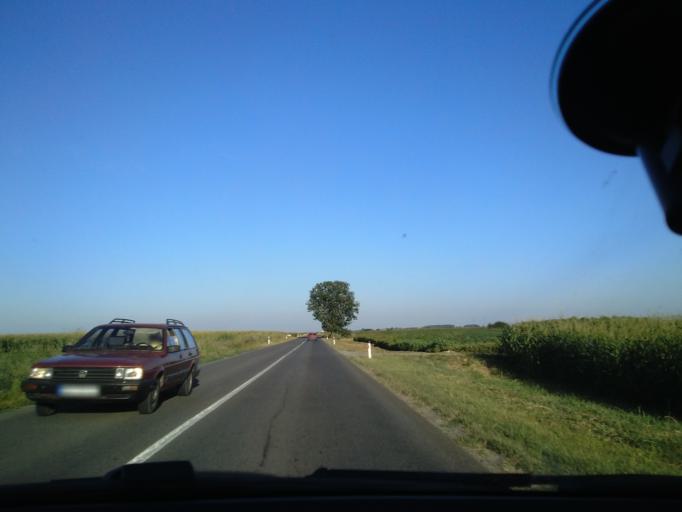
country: RS
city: Maglic
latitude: 45.3865
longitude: 19.4999
